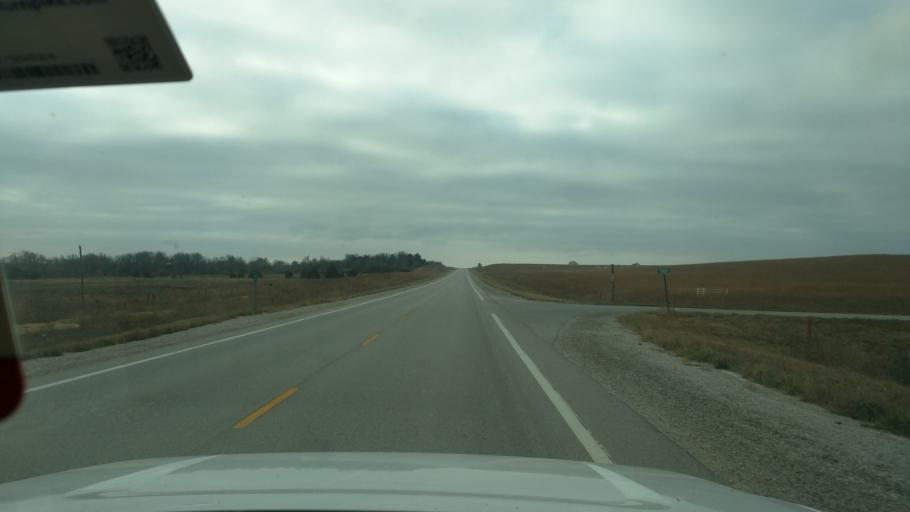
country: US
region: Kansas
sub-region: Elk County
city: Howard
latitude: 37.5922
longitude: -96.2534
